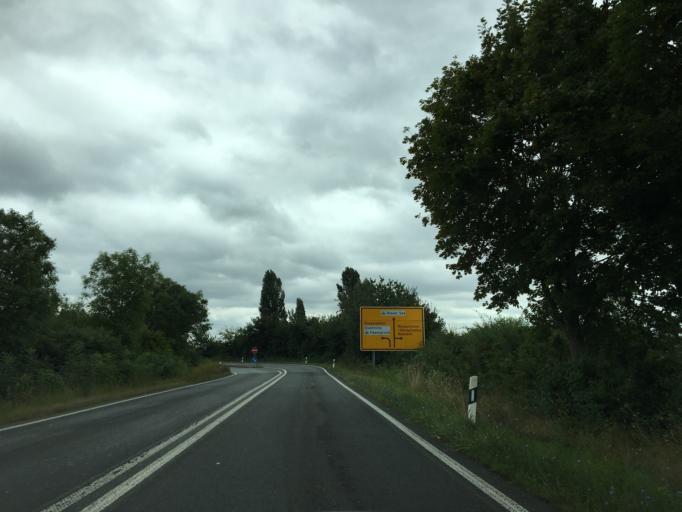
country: DE
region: Hesse
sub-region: Regierungsbezirk Darmstadt
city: Russelsheim
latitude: 49.9741
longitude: 8.4383
